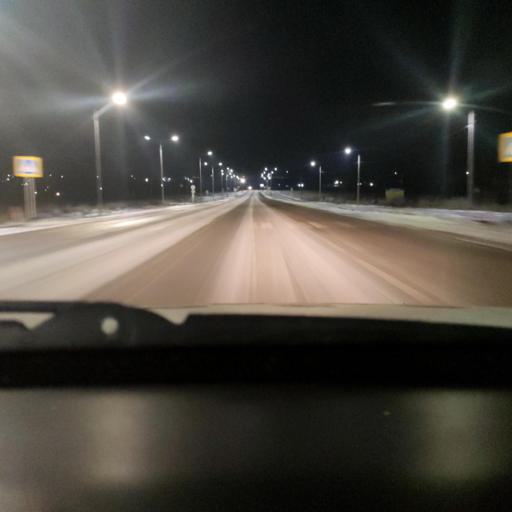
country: RU
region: Perm
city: Kultayevo
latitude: 57.8686
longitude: 55.8716
